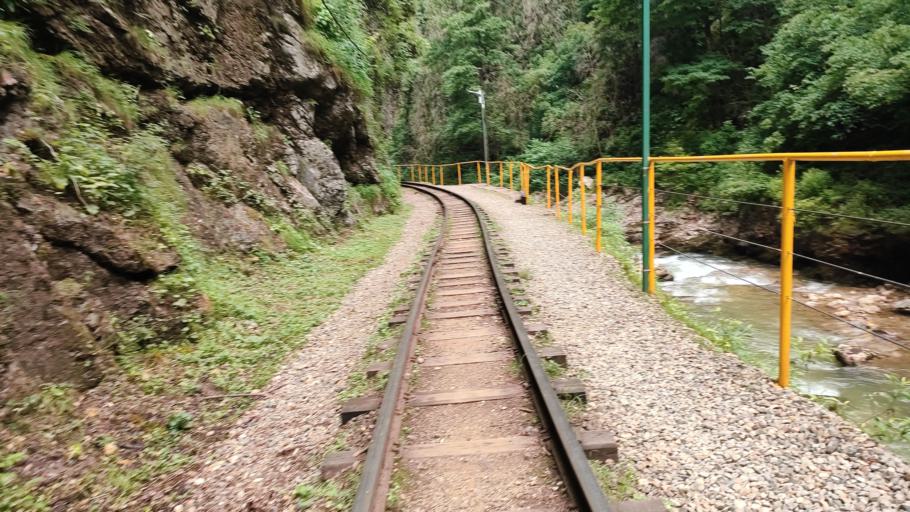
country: RU
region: Krasnodarskiy
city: Neftegorsk
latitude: 44.2191
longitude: 39.9120
